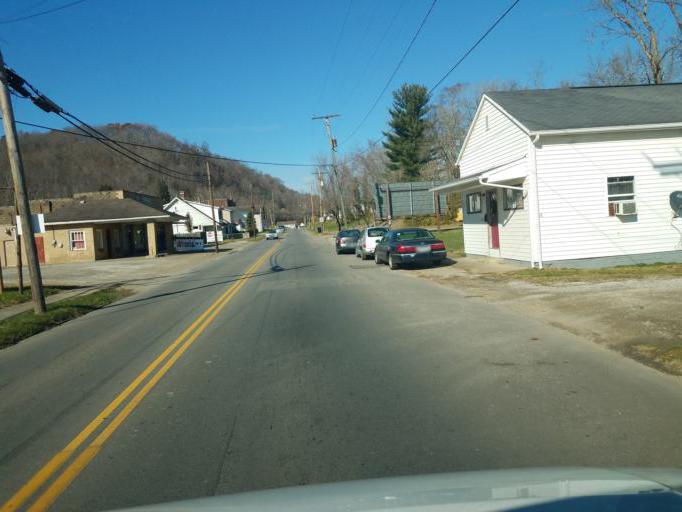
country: US
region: Ohio
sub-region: Scioto County
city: New Boston
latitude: 38.7616
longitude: -82.9342
